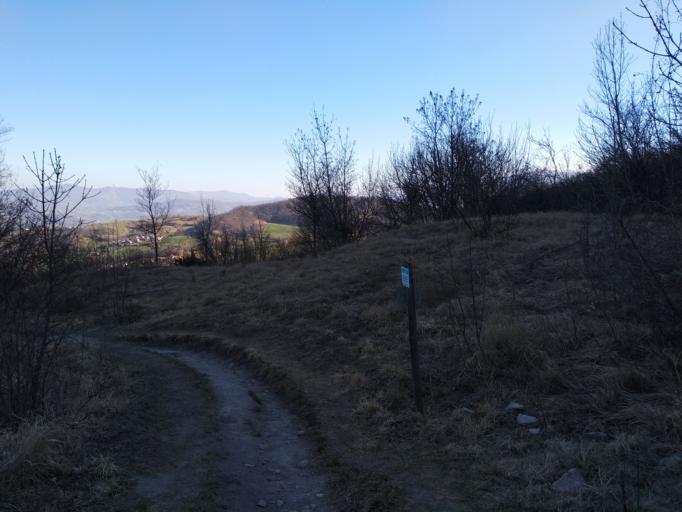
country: IT
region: Emilia-Romagna
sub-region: Provincia di Reggio Emilia
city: Castelnovo ne'Monti
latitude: 44.4248
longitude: 10.4191
